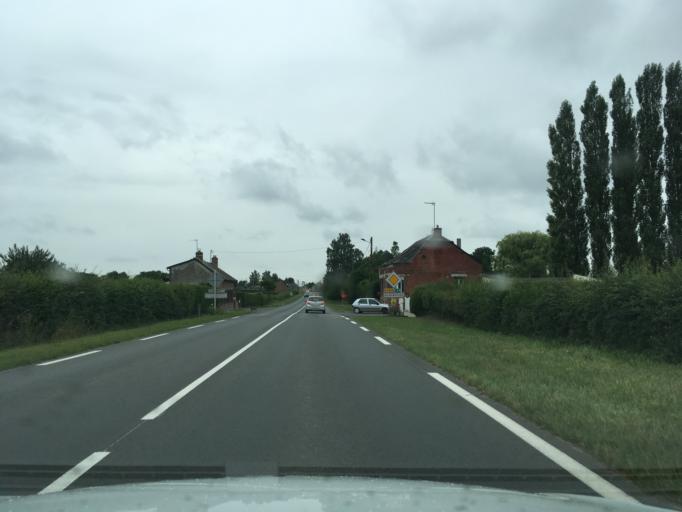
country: FR
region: Picardie
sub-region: Departement de l'Aisne
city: Buironfosse
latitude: 49.9663
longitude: 3.8459
